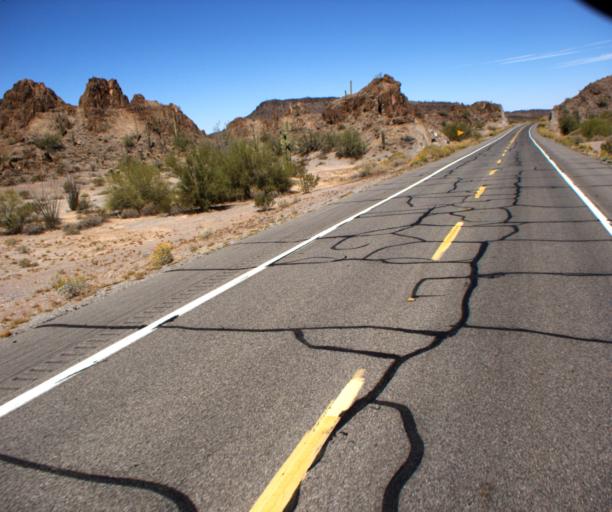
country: US
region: Arizona
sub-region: Pima County
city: Ajo
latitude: 32.5469
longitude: -112.8800
